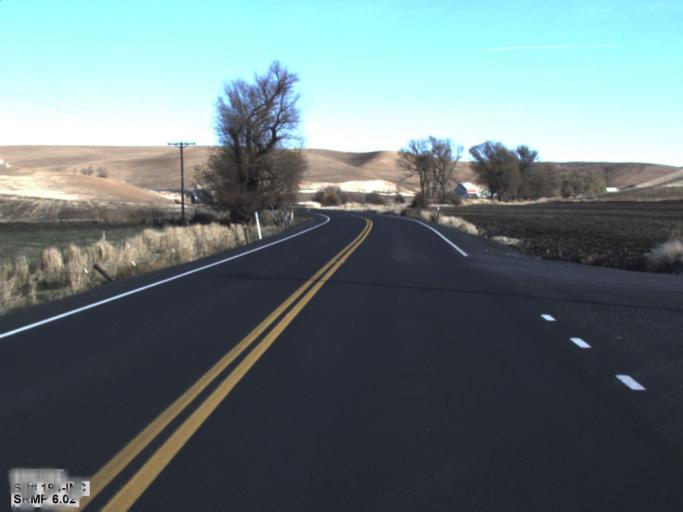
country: US
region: Washington
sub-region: Whitman County
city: Colfax
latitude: 46.7499
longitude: -117.4588
